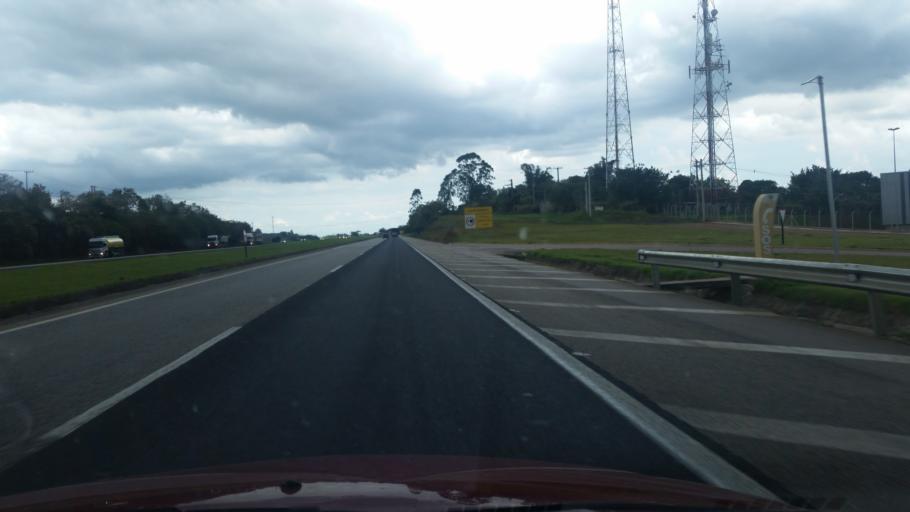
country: BR
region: Sao Paulo
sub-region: Porto Feliz
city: Porto Feliz
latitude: -23.3524
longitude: -47.5125
